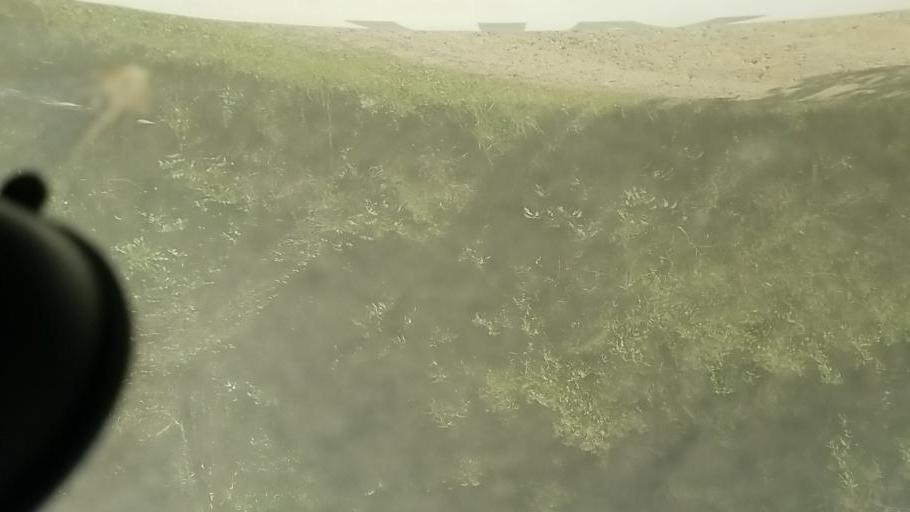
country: CD
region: Nord Kivu
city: Sake
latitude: -1.9717
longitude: 28.9139
